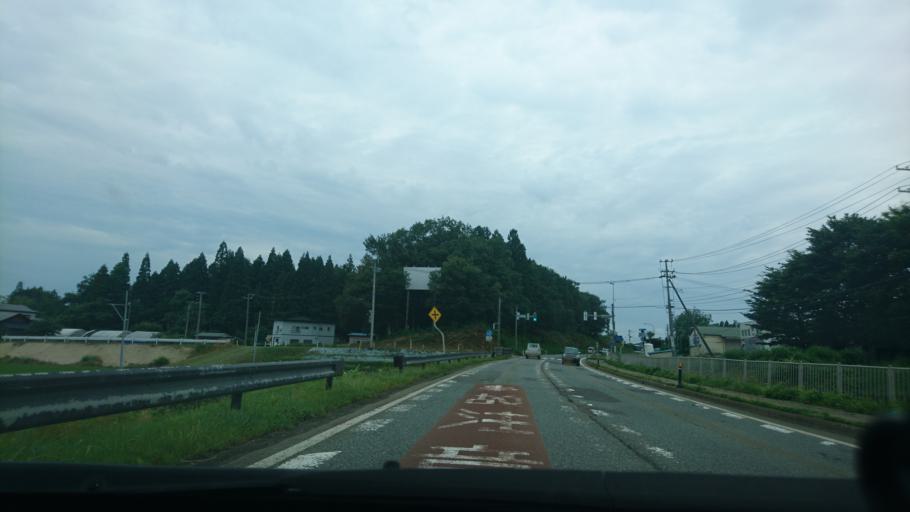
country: JP
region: Akita
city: Yokotemachi
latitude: 39.3420
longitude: 140.5595
